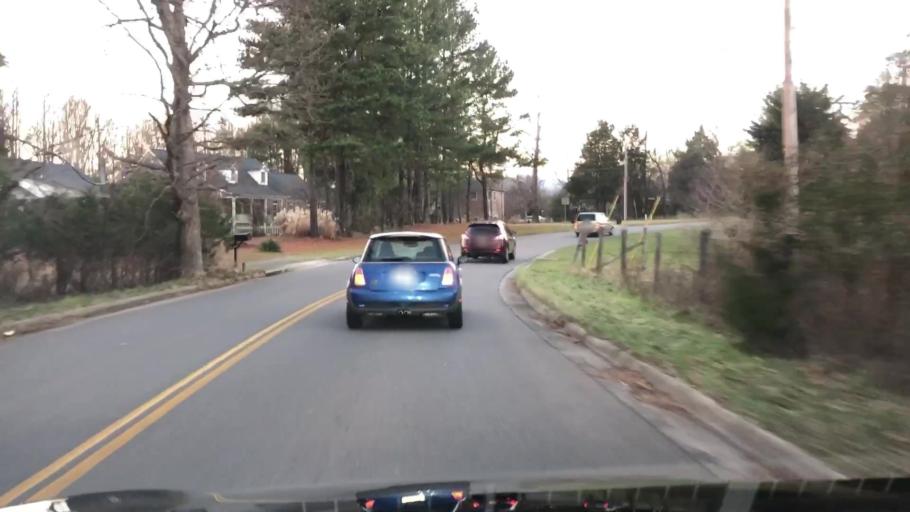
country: US
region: Virginia
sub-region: City of Lynchburg
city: West Lynchburg
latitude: 37.4216
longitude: -79.2461
